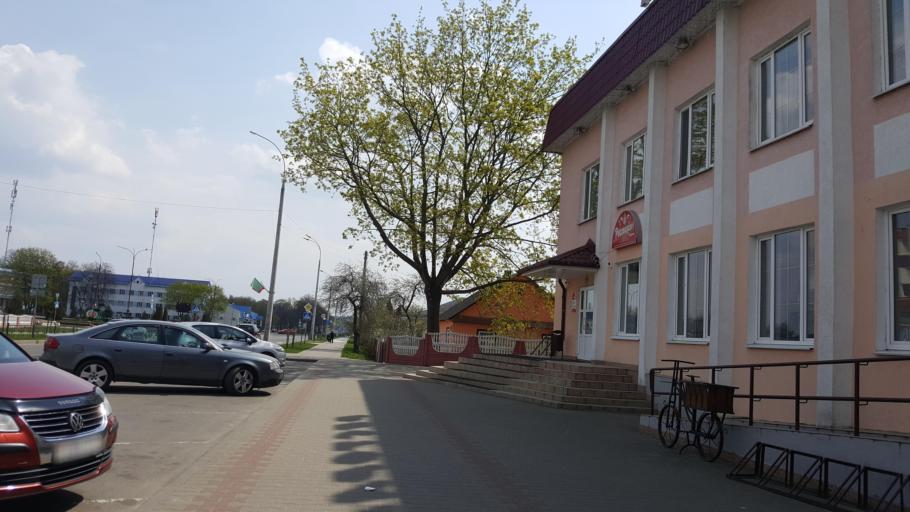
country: BY
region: Brest
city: Zhabinka
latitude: 52.1943
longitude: 24.0178
